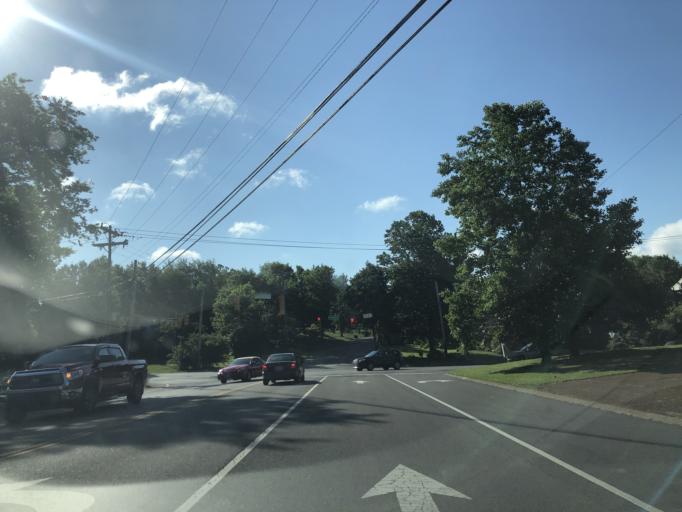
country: US
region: Tennessee
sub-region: Davidson County
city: Belle Meade
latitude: 36.0625
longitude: -86.9433
